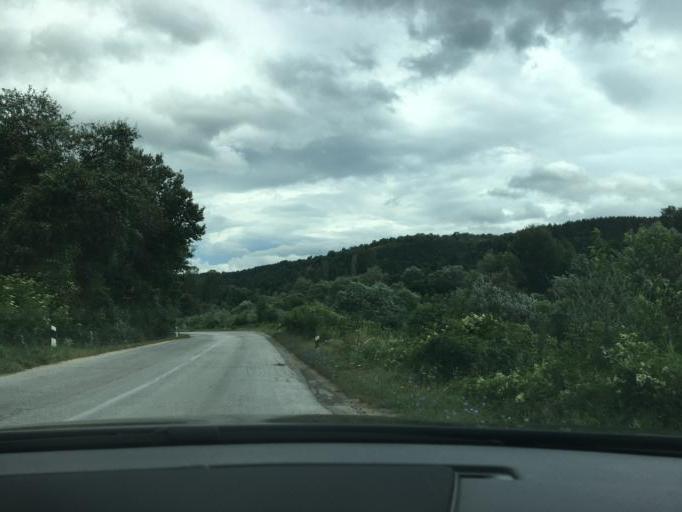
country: MK
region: Kriva Palanka
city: Kriva Palanka
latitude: 42.1892
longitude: 22.2963
